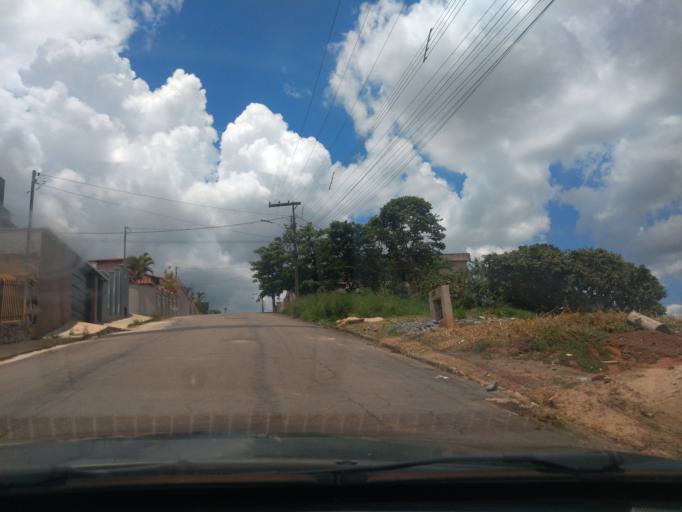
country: BR
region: Minas Gerais
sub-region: Tres Coracoes
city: Tres Coracoes
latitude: -21.6952
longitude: -45.2643
